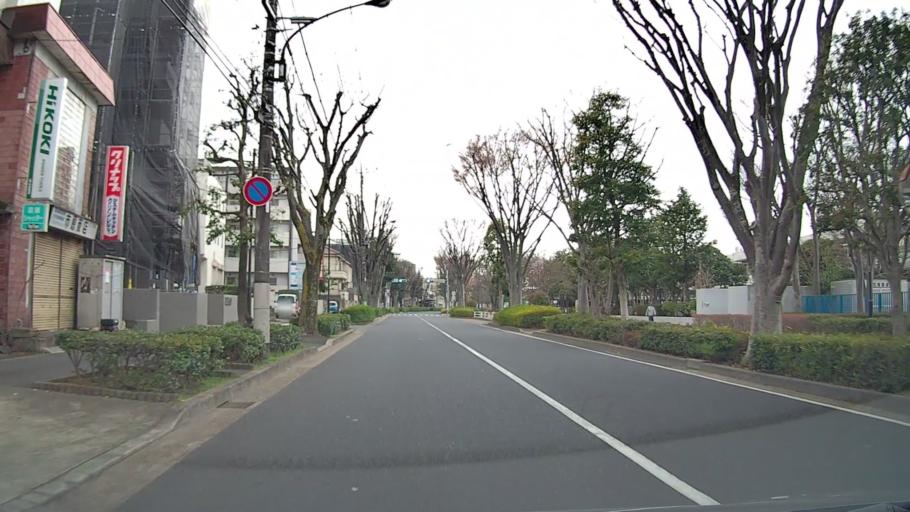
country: JP
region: Saitama
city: Asaka
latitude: 35.7757
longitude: 139.5934
